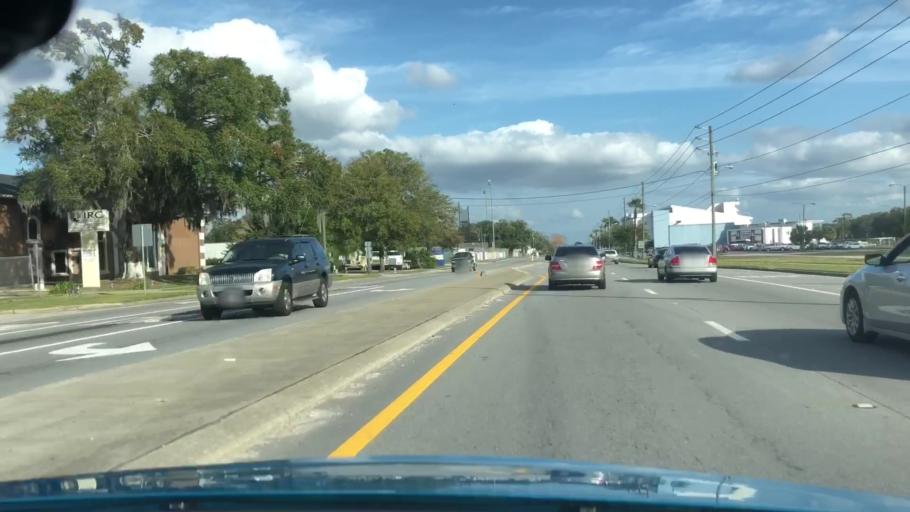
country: US
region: Florida
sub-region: Seminole County
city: Casselberry
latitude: 28.6838
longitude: -81.3463
